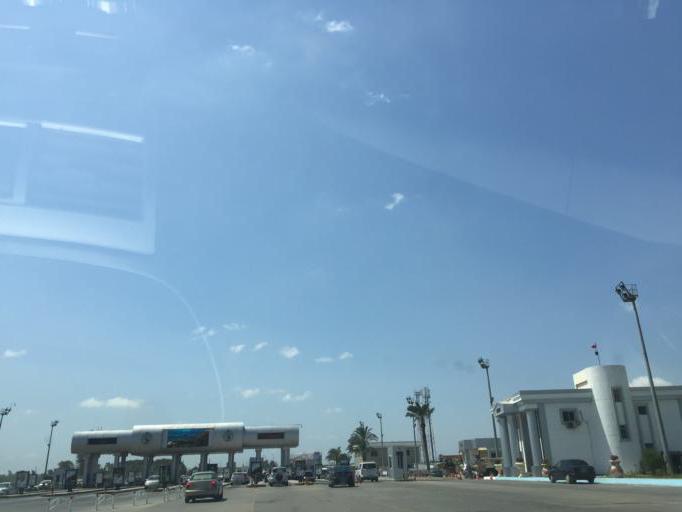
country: EG
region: Alexandria
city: Alexandria
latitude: 30.9686
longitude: 29.8287
